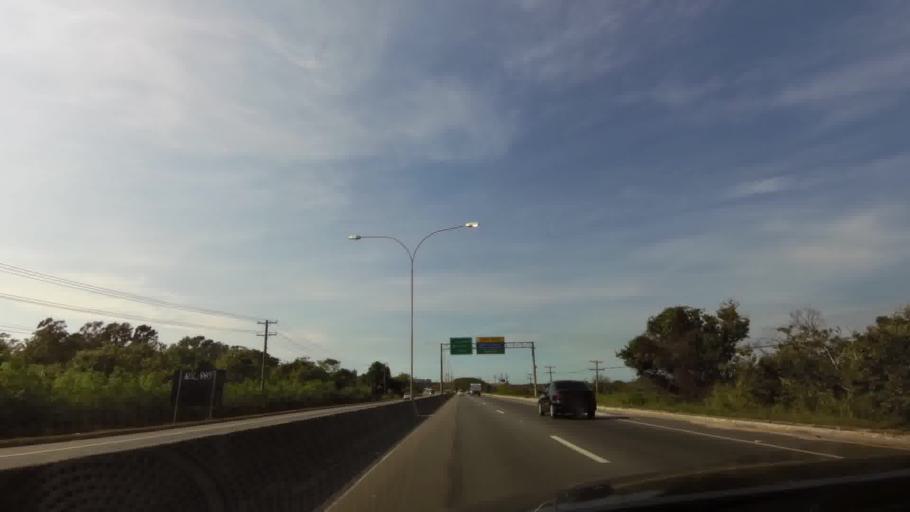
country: BR
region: Espirito Santo
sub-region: Vila Velha
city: Vila Velha
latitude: -20.3986
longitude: -40.3218
